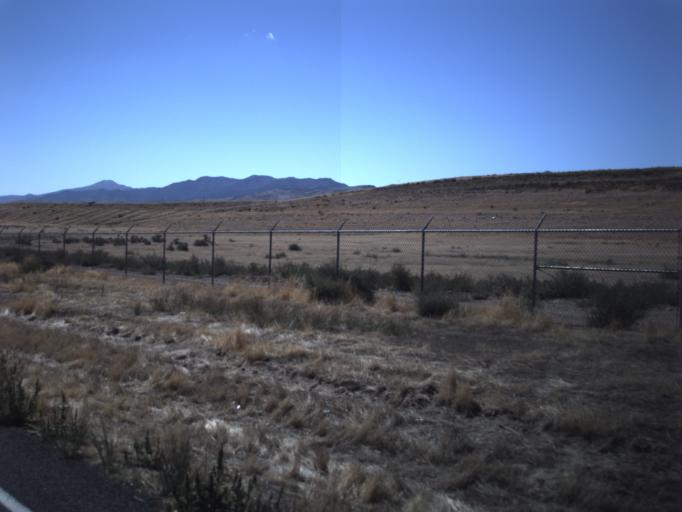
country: US
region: Utah
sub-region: Utah County
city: Genola
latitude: 40.0296
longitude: -111.9583
